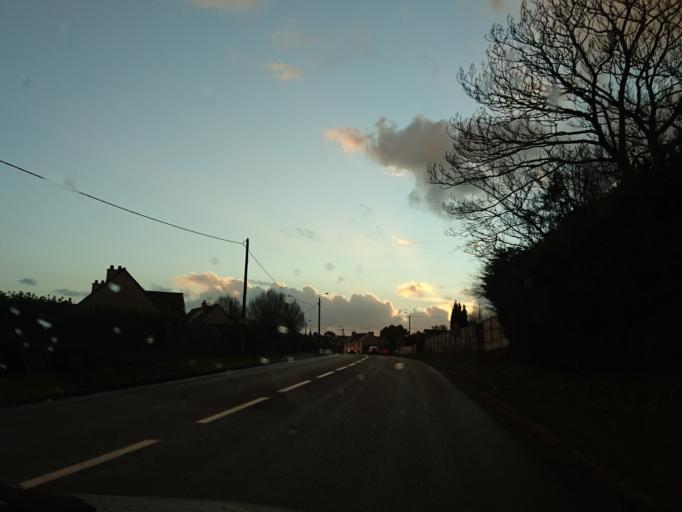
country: FR
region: Brittany
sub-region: Departement du Finistere
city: Guipavas
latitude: 48.4423
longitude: -4.3925
